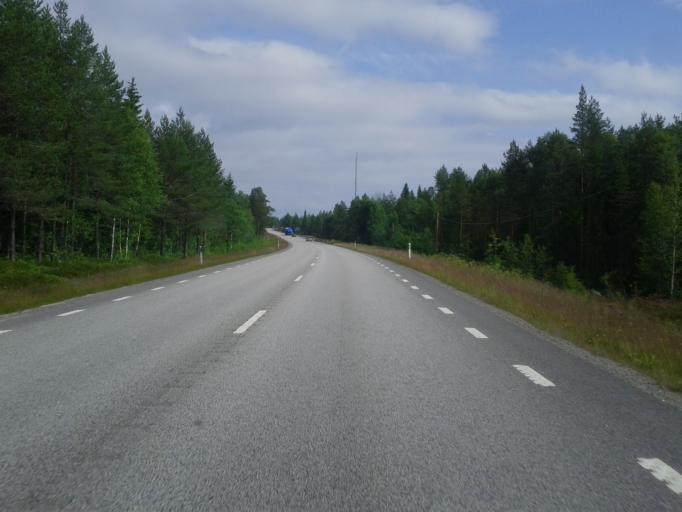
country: SE
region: Vaesterbotten
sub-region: Robertsfors Kommun
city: Robertsfors
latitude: 64.1864
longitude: 20.9940
